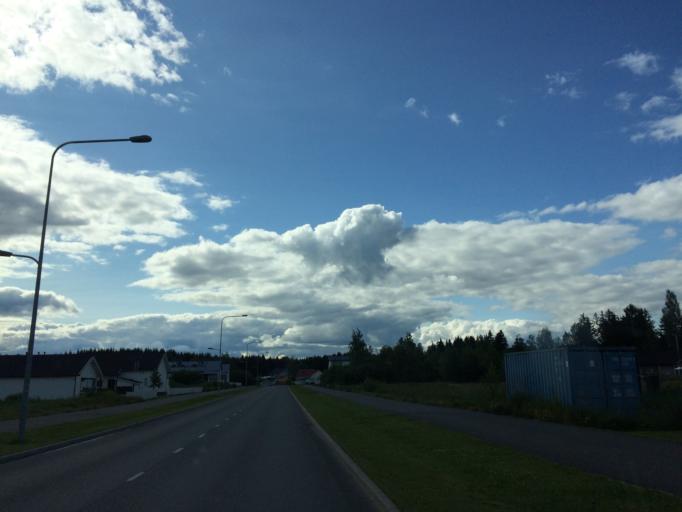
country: FI
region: Haeme
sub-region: Haemeenlinna
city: Parola
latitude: 60.9769
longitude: 24.3753
